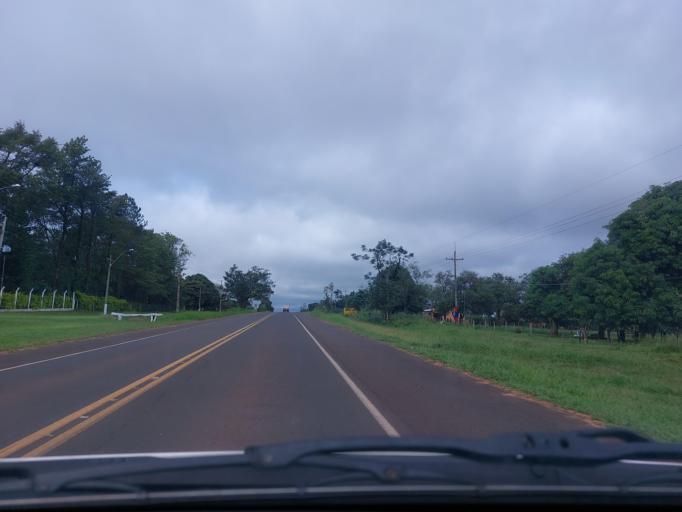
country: PY
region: San Pedro
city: Guayaybi
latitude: -24.6078
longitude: -56.3824
